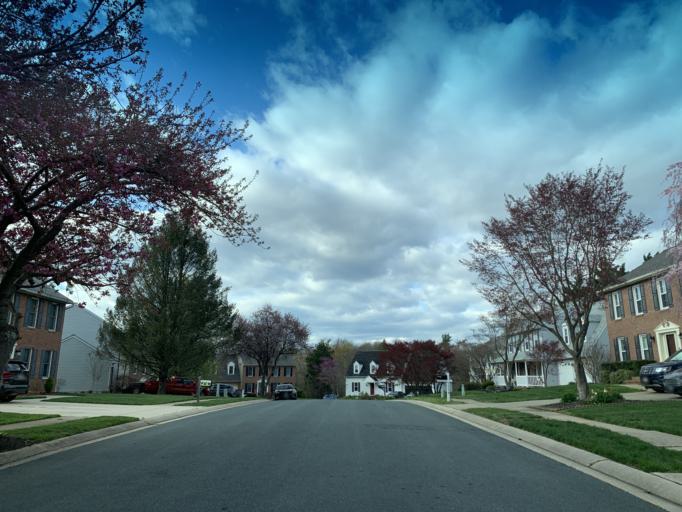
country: US
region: Maryland
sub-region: Harford County
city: South Bel Air
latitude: 39.5496
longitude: -76.3224
